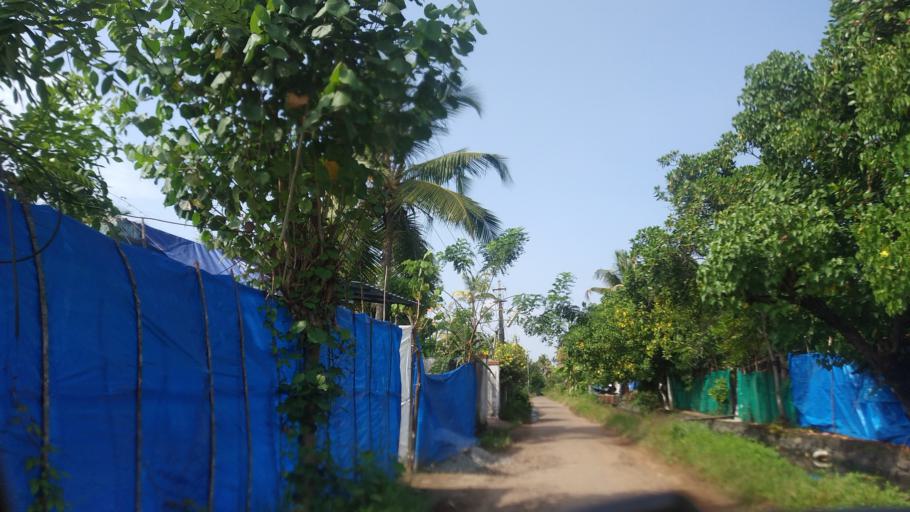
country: IN
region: Kerala
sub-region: Ernakulam
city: Elur
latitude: 10.0806
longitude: 76.2037
